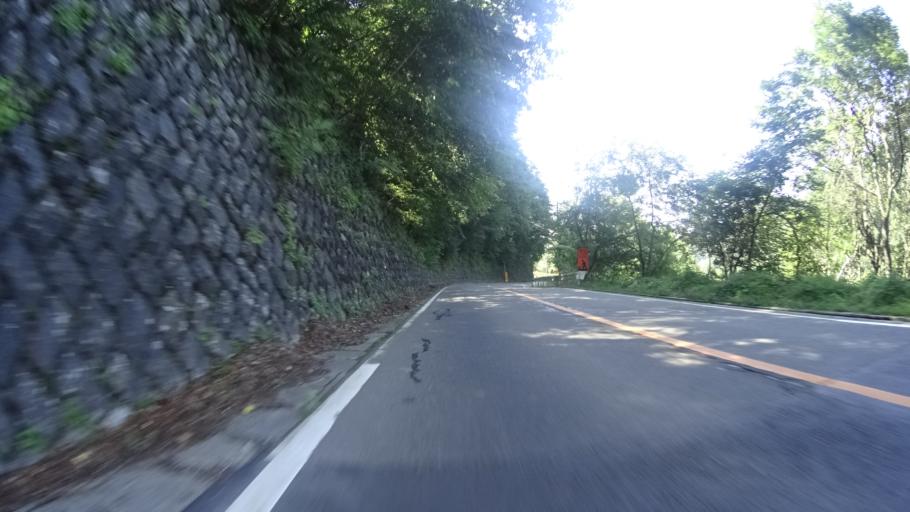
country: JP
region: Yamanashi
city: Enzan
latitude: 35.7730
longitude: 138.8047
